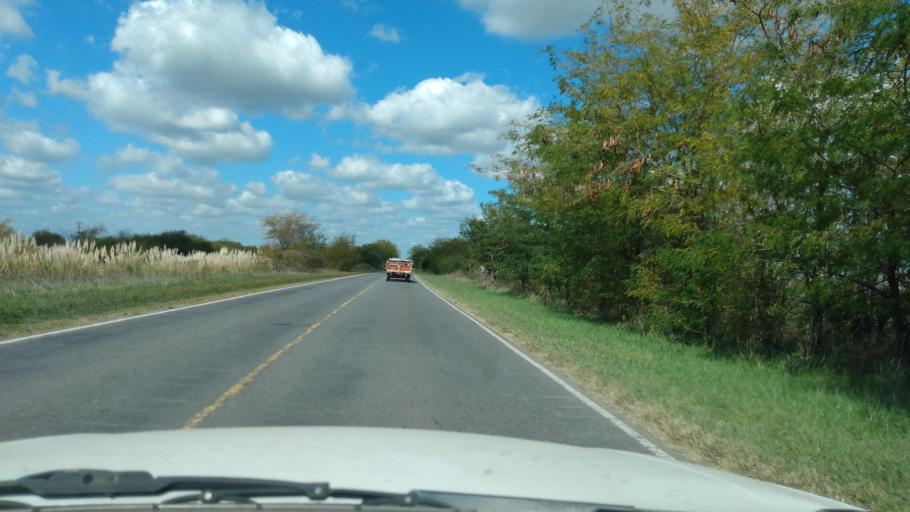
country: AR
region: Buenos Aires
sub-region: Partido de Navarro
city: Navarro
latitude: -34.9404
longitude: -59.3214
